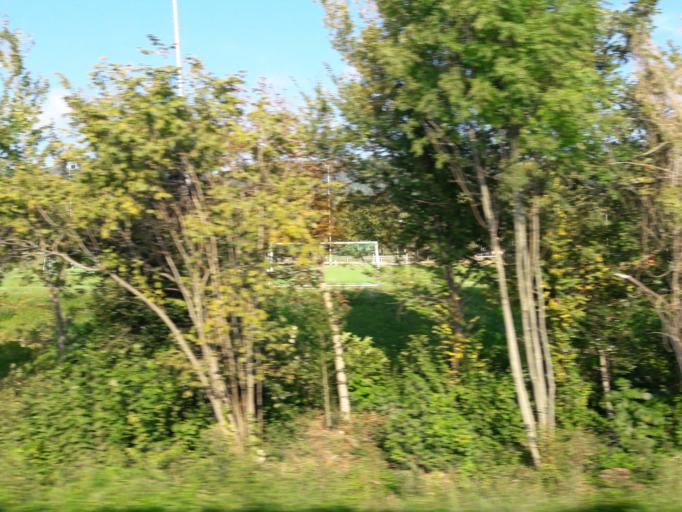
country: CH
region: Vaud
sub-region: Nyon District
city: Rolle
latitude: 46.4571
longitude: 6.3281
